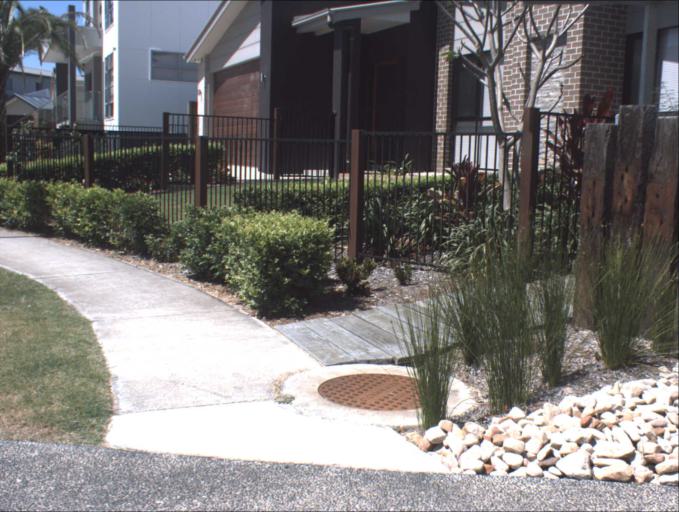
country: AU
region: Queensland
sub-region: Logan
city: Windaroo
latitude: -27.7440
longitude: 153.1974
